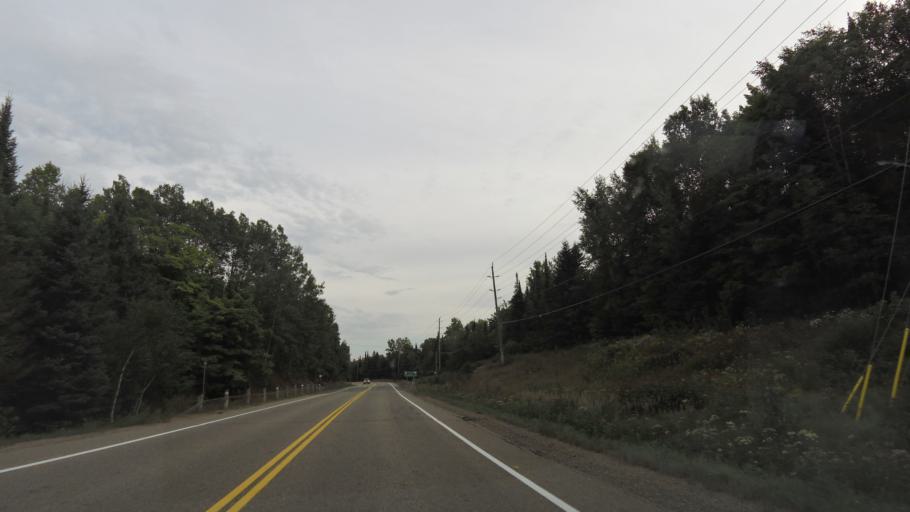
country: CA
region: Ontario
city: Bancroft
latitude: 45.0345
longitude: -78.4556
